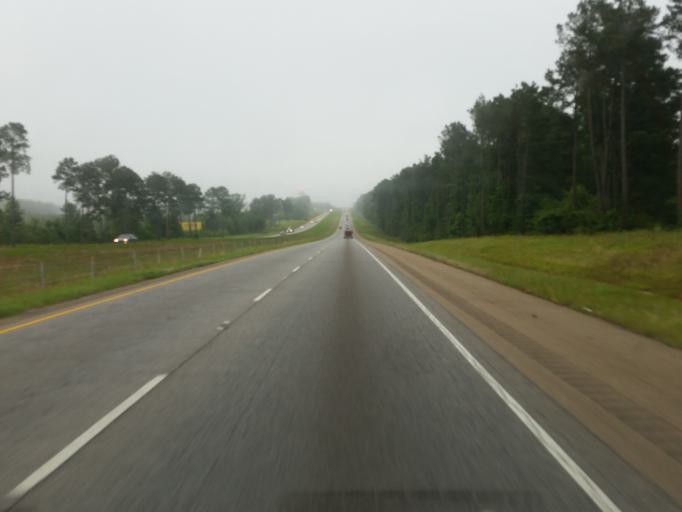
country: US
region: Louisiana
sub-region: Webster Parish
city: Minden
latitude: 32.5837
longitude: -93.2640
